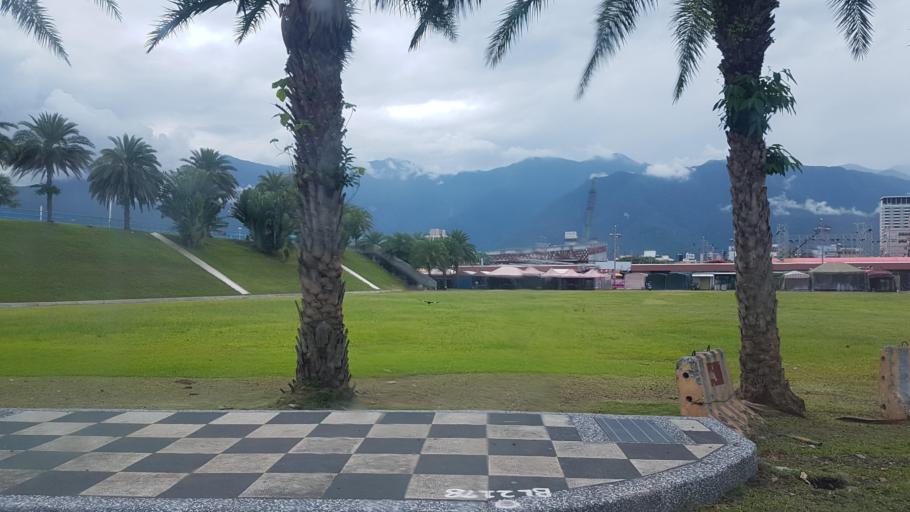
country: TW
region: Taiwan
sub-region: Hualien
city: Hualian
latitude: 23.9712
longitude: 121.6131
